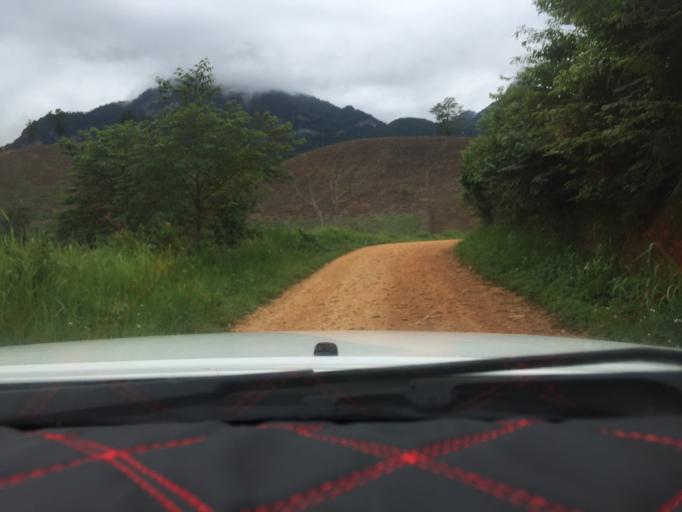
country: TH
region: Phayao
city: Phu Sang
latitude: 19.7703
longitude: 100.4961
